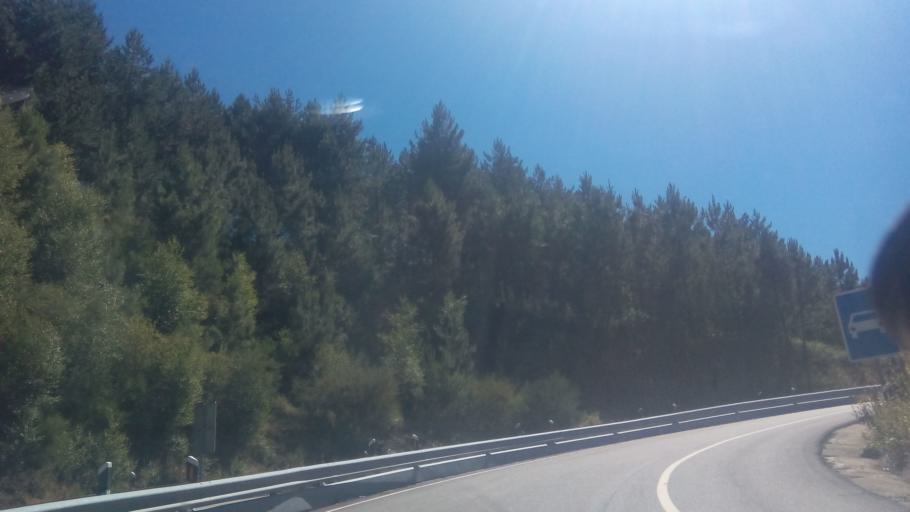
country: PT
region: Vila Real
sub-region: Santa Marta de Penaguiao
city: Santa Marta de Penaguiao
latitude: 41.2808
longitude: -7.8420
